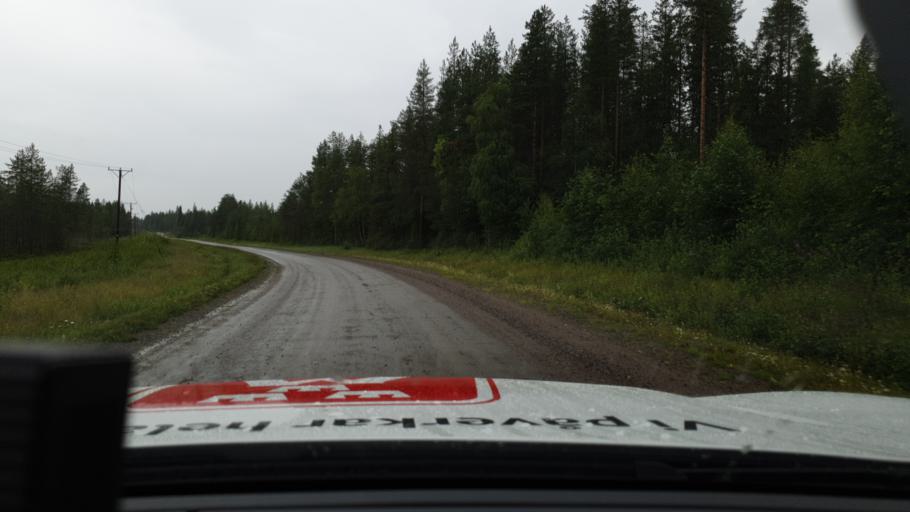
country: SE
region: Norrbotten
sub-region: Bodens Kommun
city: Boden
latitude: 66.3050
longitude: 21.3045
